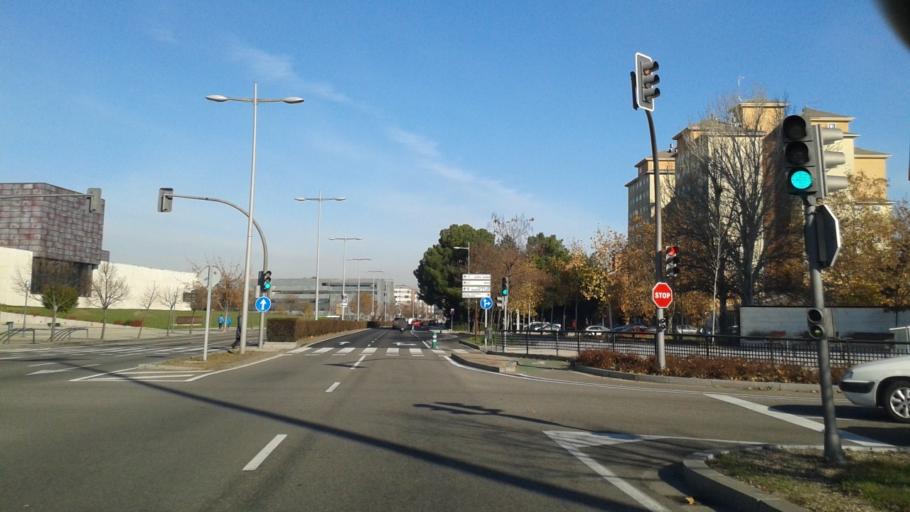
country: ES
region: Castille and Leon
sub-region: Provincia de Valladolid
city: Valladolid
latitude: 41.6414
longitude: -4.7444
